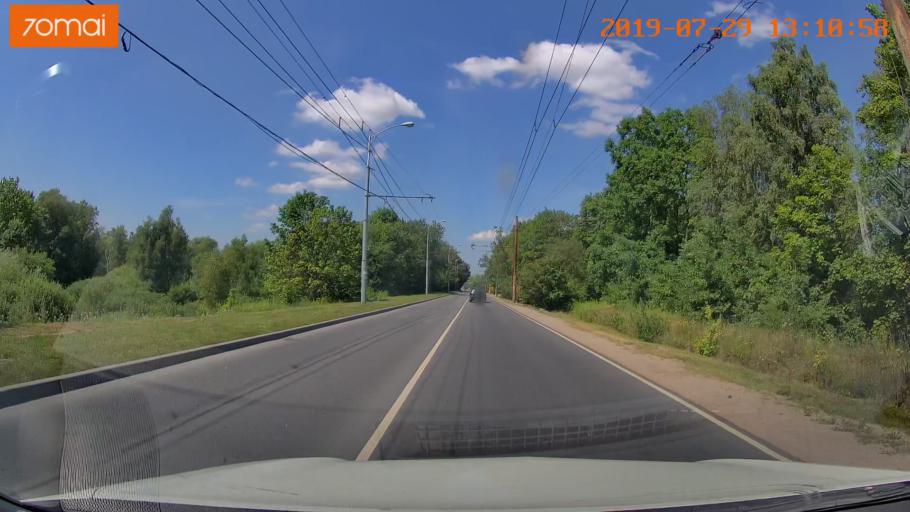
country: RU
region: Kaliningrad
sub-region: Gorod Kaliningrad
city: Kaliningrad
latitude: 54.7174
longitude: 20.3951
